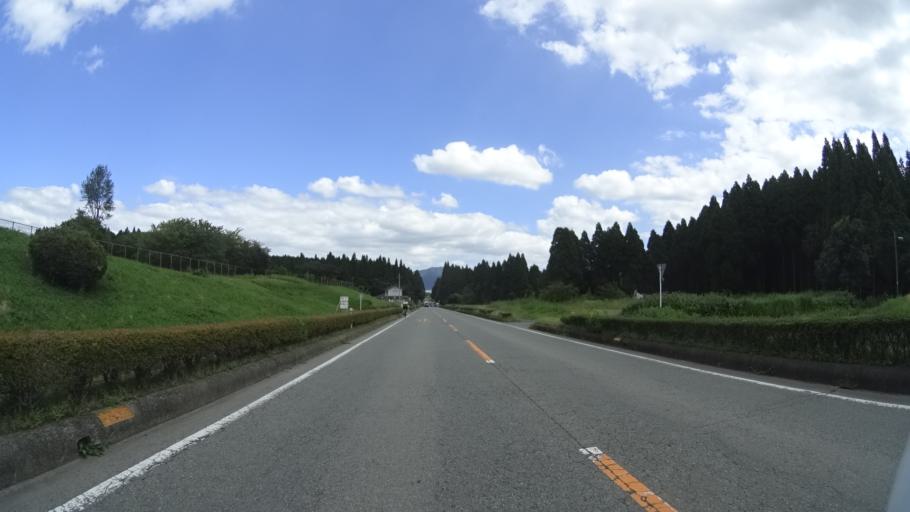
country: JP
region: Kumamoto
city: Aso
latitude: 32.8315
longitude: 131.0819
